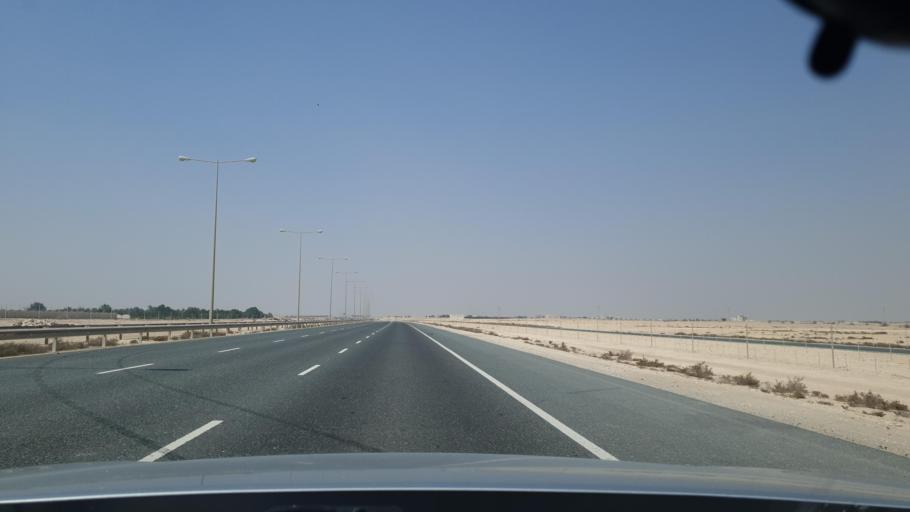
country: QA
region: Al Khawr
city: Al Khawr
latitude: 25.7724
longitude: 51.4125
